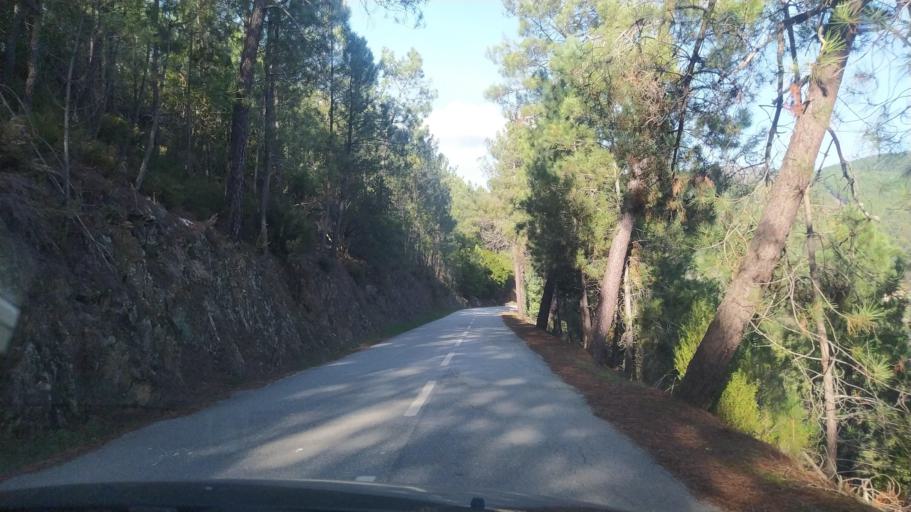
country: PT
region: Coimbra
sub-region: Oliveira do Hospital
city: Oliveira do Hospital
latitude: 40.2021
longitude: -7.7354
